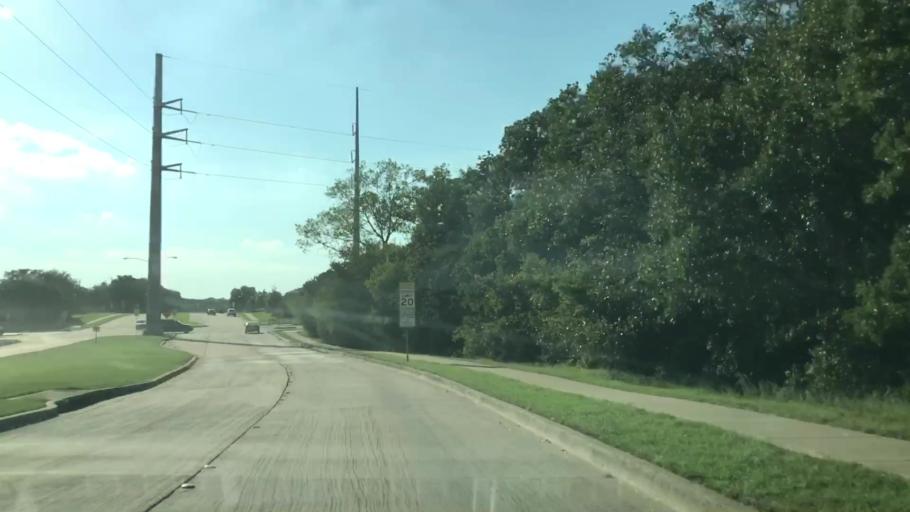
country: US
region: Texas
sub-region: Denton County
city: Lewisville
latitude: 33.0326
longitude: -97.0348
